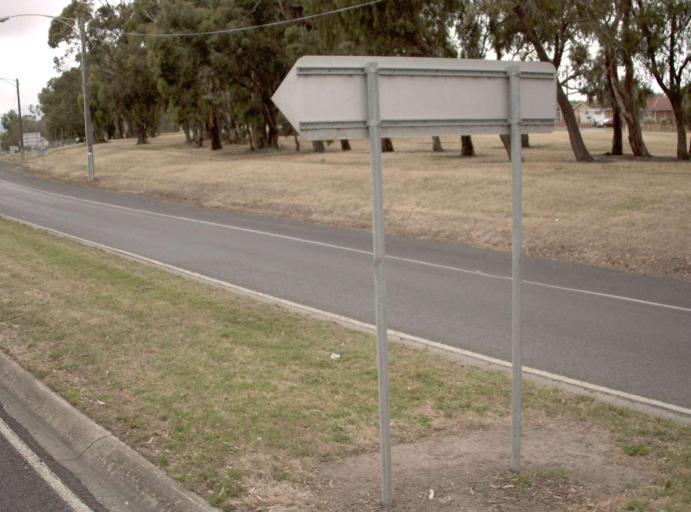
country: AU
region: Victoria
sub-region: Latrobe
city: Morwell
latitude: -38.3064
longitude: 146.4209
